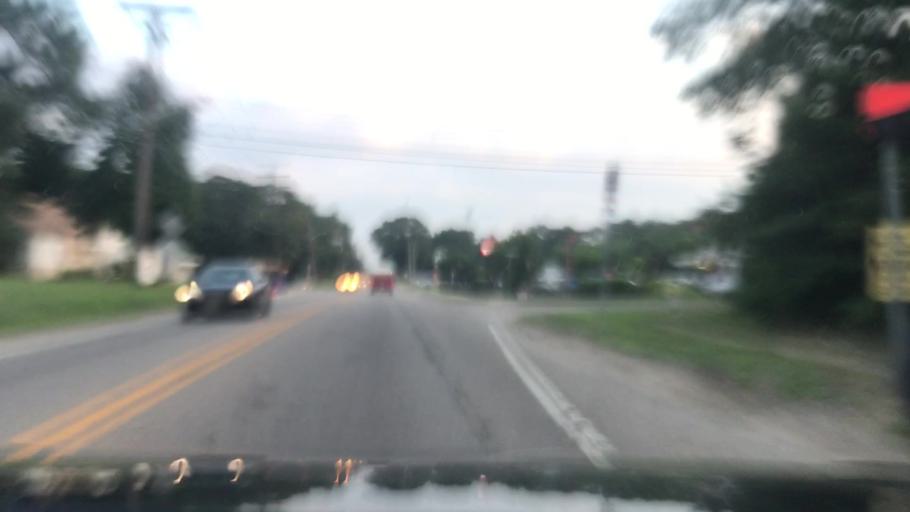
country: US
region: New Jersey
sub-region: Ocean County
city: Silver Ridge
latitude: 39.9979
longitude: -74.2120
